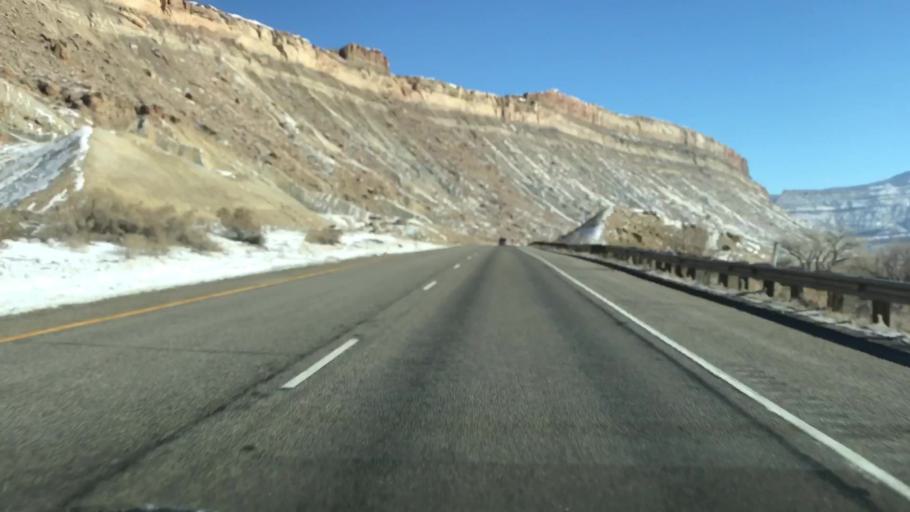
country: US
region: Colorado
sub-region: Mesa County
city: Palisade
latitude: 39.1196
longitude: -108.3793
